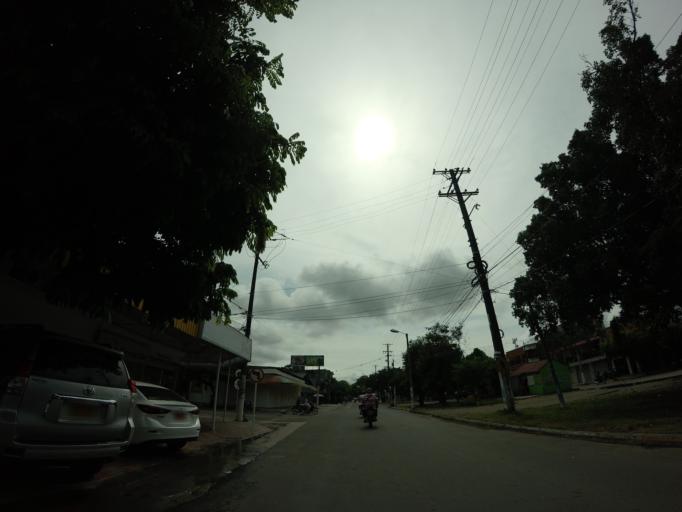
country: CO
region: Caldas
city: La Dorada
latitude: 5.4486
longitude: -74.6646
